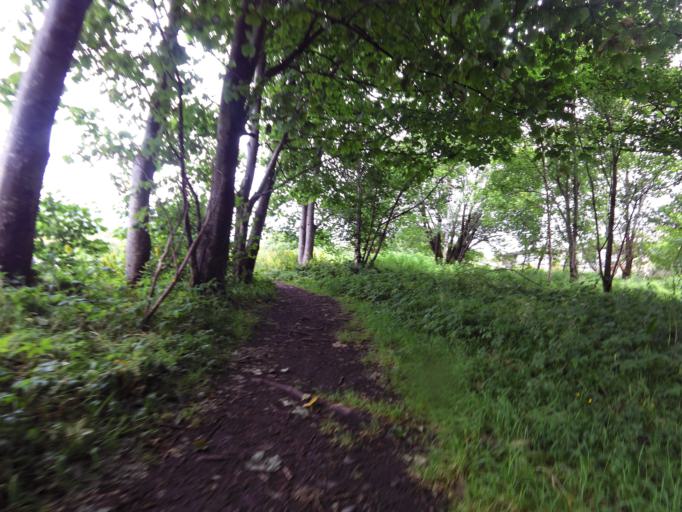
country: GB
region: Scotland
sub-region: Highland
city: Fort William
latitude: 56.8251
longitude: -5.1000
